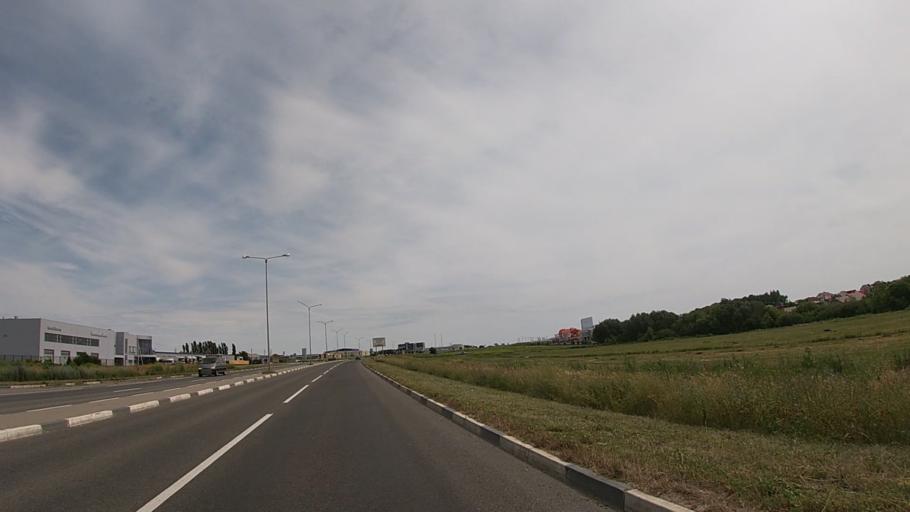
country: RU
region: Belgorod
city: Severnyy
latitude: 50.6578
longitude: 36.5481
